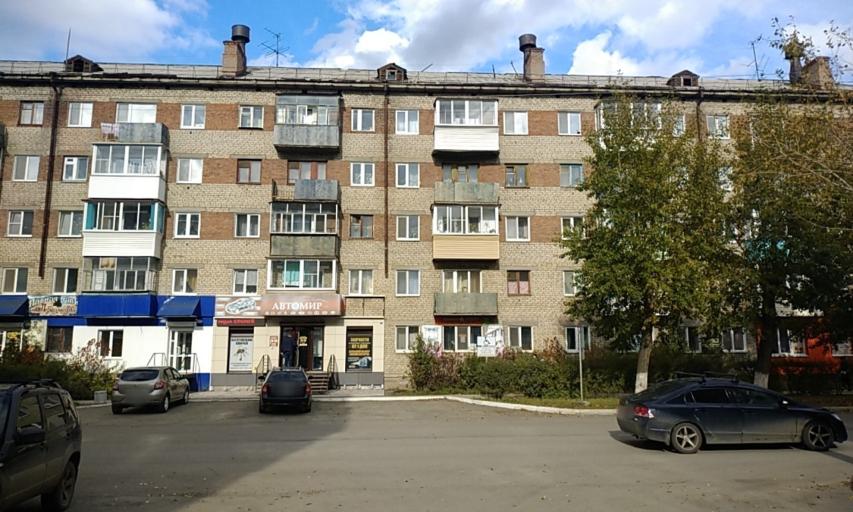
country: RU
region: Sverdlovsk
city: Krasnoural'sk
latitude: 58.3558
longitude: 60.0431
